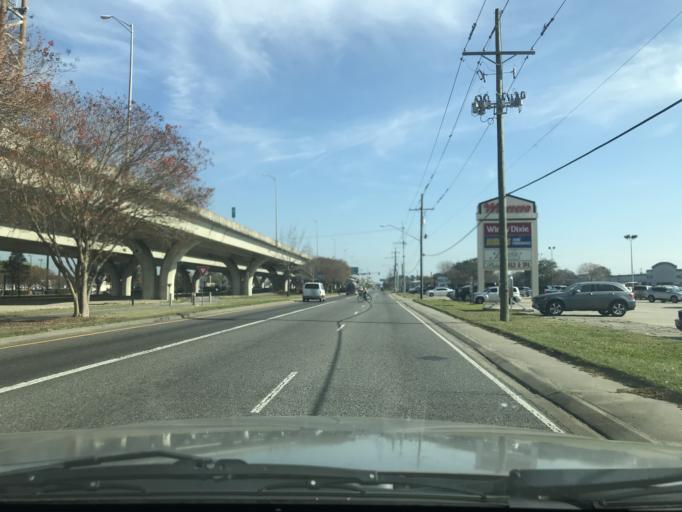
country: US
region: Louisiana
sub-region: Jefferson Parish
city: Marrero
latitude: 29.8945
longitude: -90.0980
